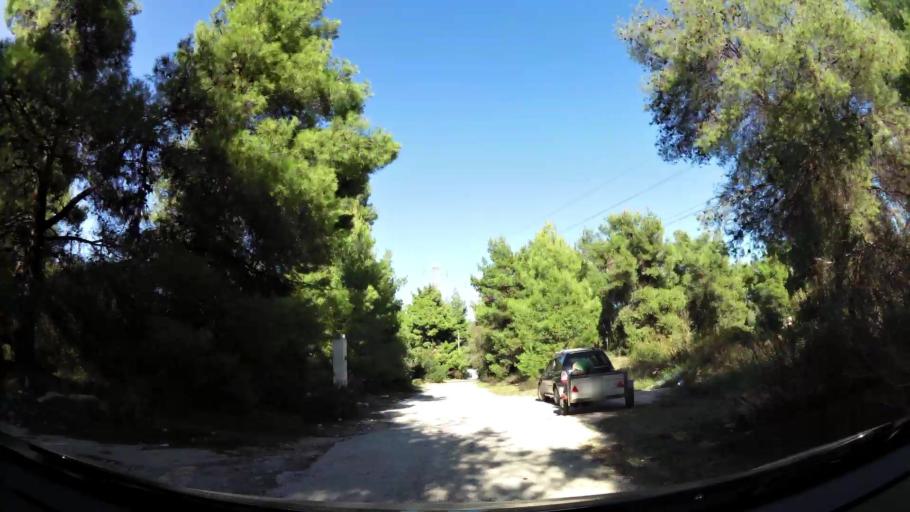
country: GR
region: Attica
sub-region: Nomarchia Anatolikis Attikis
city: Drosia
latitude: 38.1101
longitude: 23.8568
